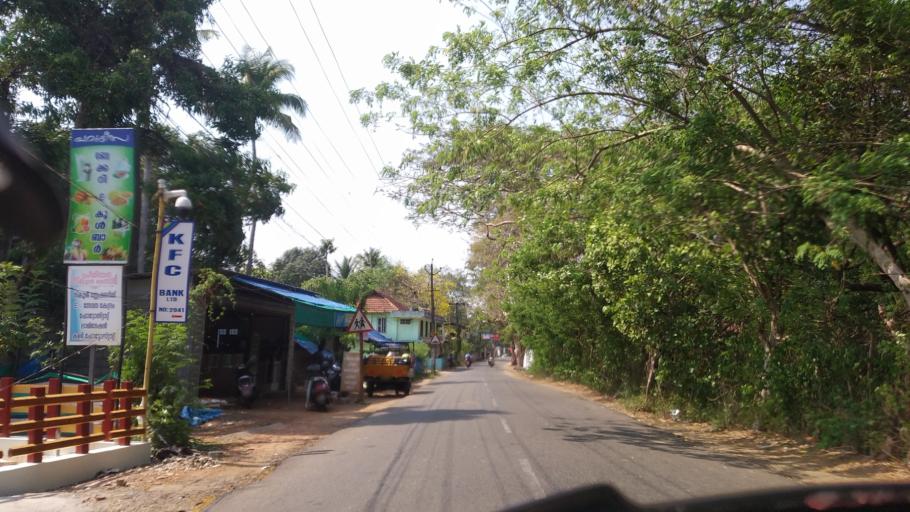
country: IN
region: Kerala
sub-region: Thrissur District
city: Irinjalakuda
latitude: 10.3158
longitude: 76.1261
